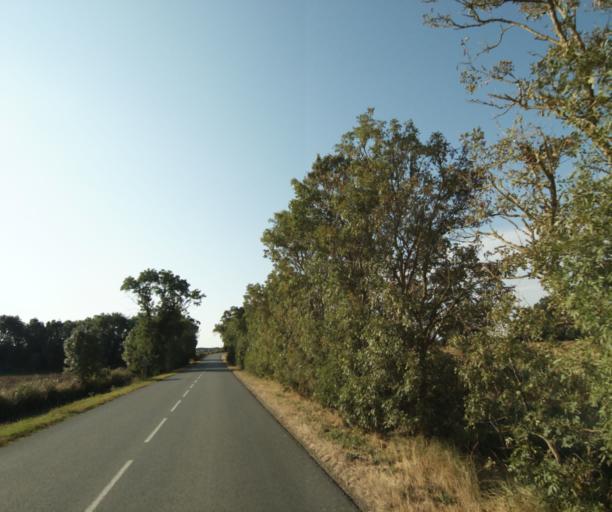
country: FR
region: Poitou-Charentes
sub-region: Departement de la Charente-Maritime
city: Muron
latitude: 45.9880
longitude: -0.8390
